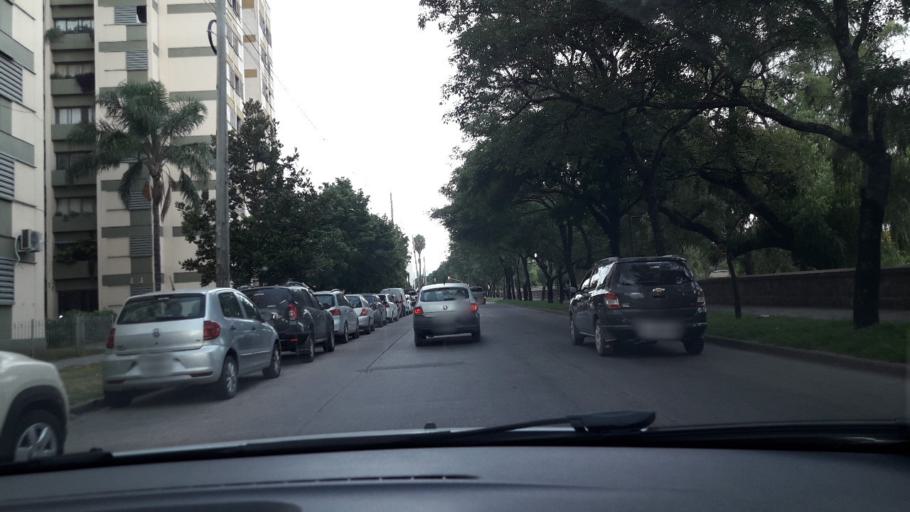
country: AR
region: Jujuy
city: San Salvador de Jujuy
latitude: -24.1907
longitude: -65.2944
